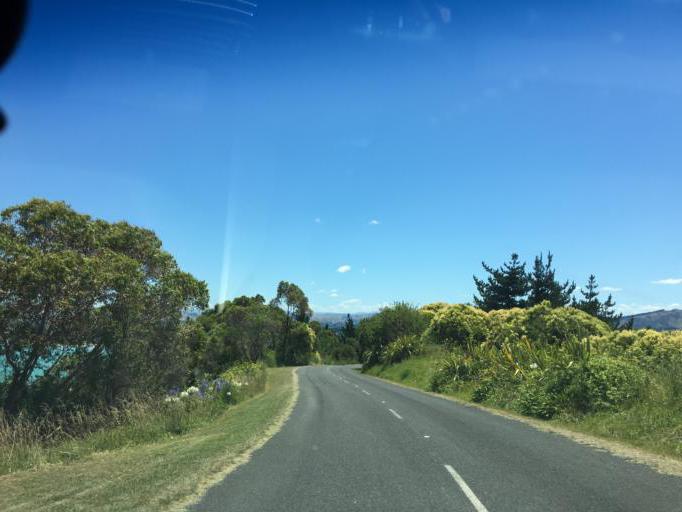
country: NZ
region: Gisborne
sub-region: Gisborne District
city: Gisborne
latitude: -38.6776
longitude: 178.0307
